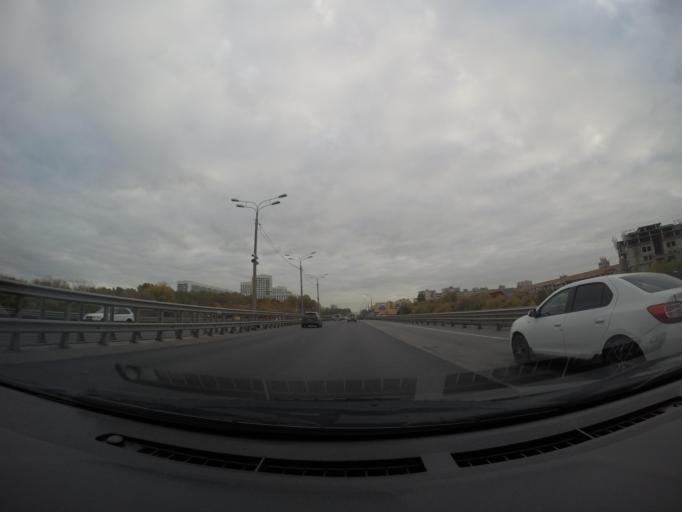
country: RU
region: Moskovskaya
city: Balashikha
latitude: 55.7953
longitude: 37.9545
